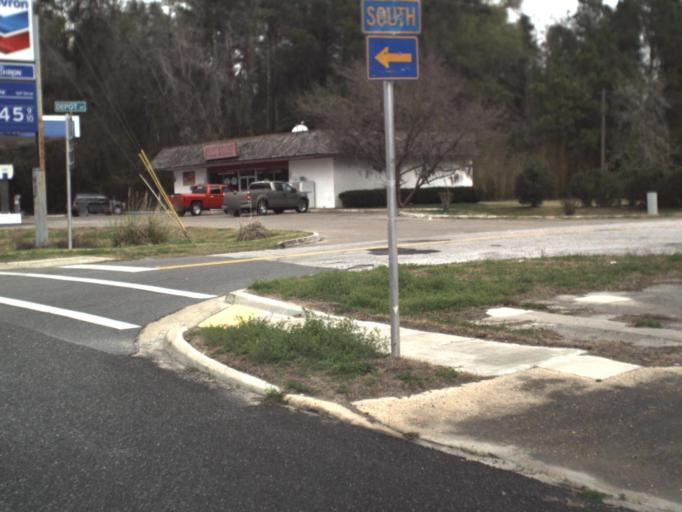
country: US
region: Florida
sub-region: Jefferson County
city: Monticello
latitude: 30.3772
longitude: -83.8126
